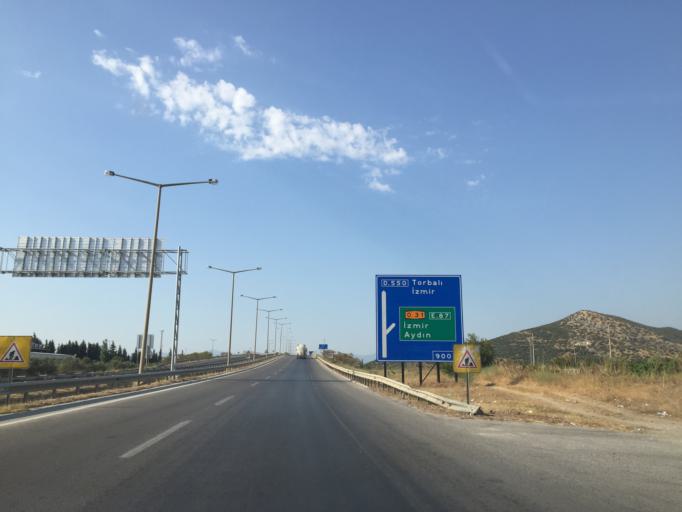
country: TR
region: Izmir
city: Belevi
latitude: 38.0221
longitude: 27.4414
